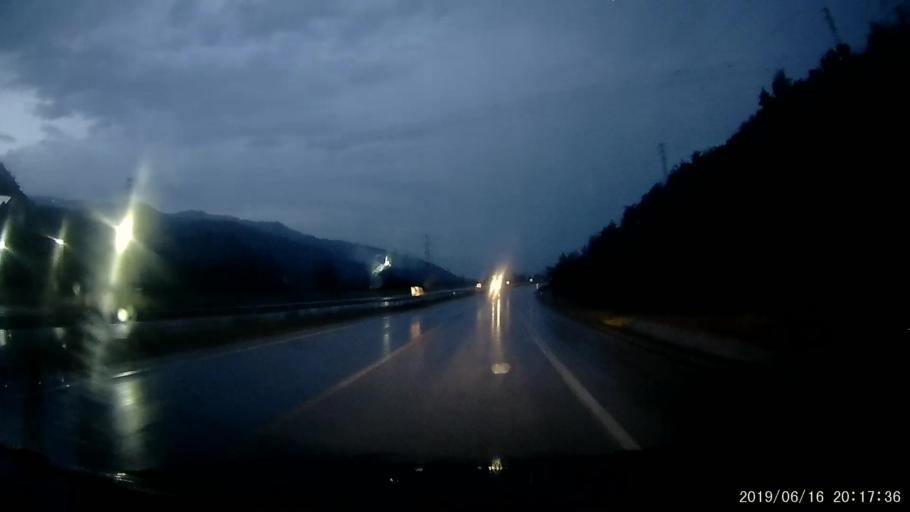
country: TR
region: Tokat
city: Resadiye
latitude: 40.3657
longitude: 37.4193
